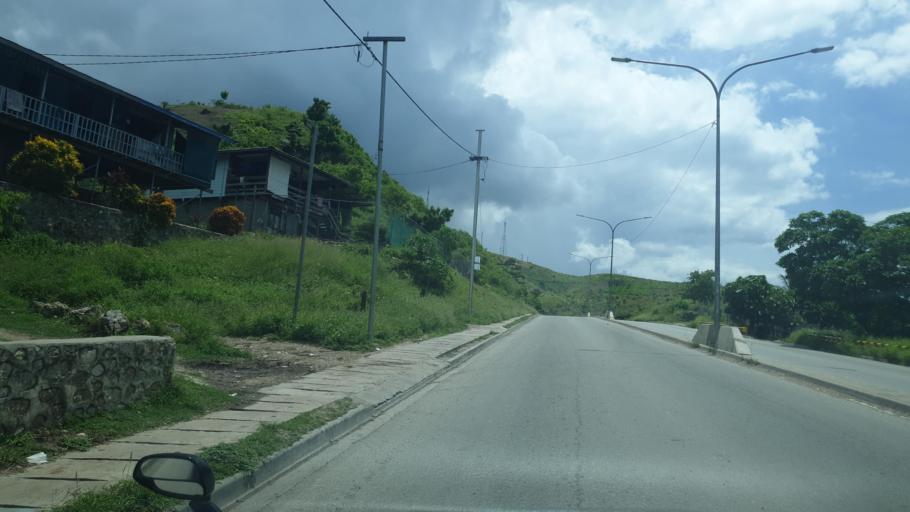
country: PG
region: National Capital
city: Port Moresby
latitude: -9.4522
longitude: 147.1553
